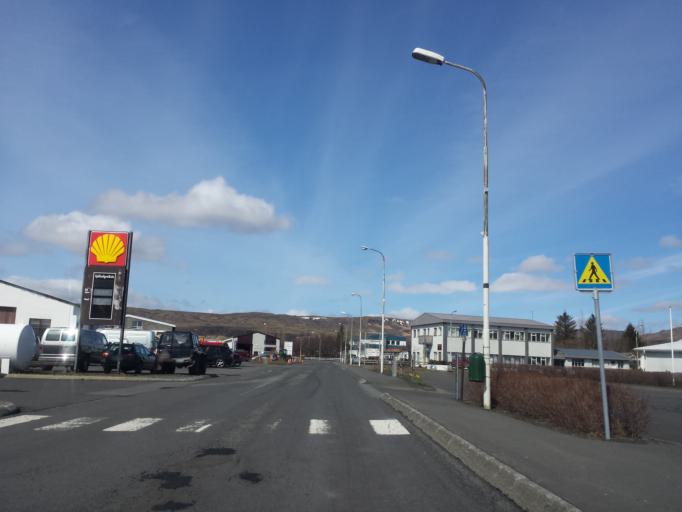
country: IS
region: South
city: Hveragerdi
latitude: 63.9957
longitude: -21.1849
